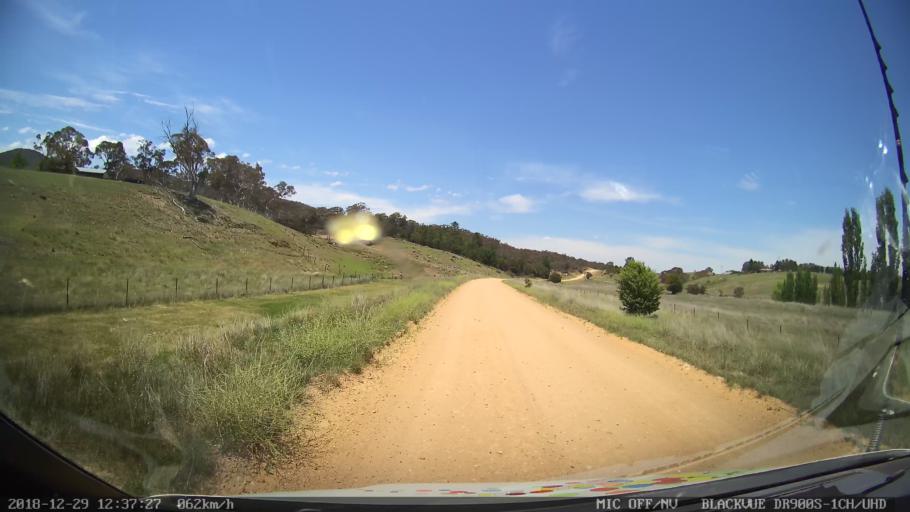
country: AU
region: Australian Capital Territory
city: Macarthur
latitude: -35.5802
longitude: 149.2282
